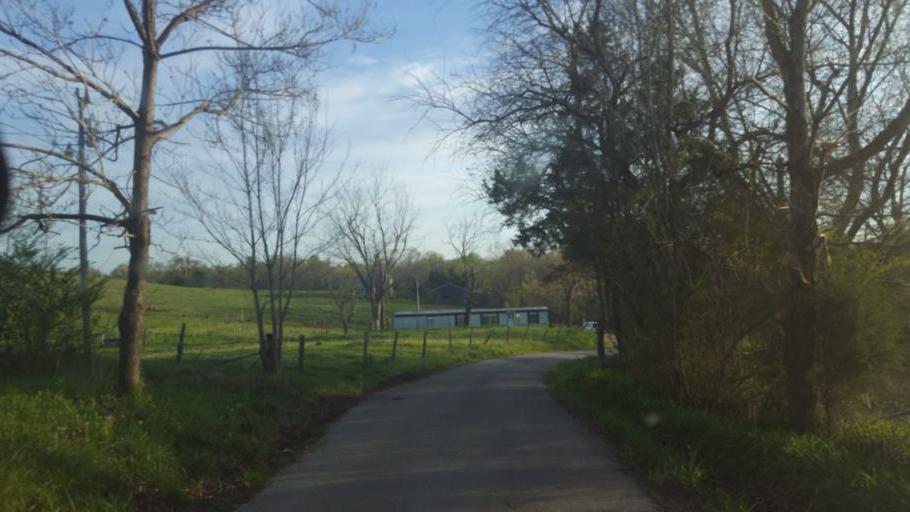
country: US
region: Kentucky
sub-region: Barren County
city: Cave City
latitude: 37.2151
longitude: -86.0006
